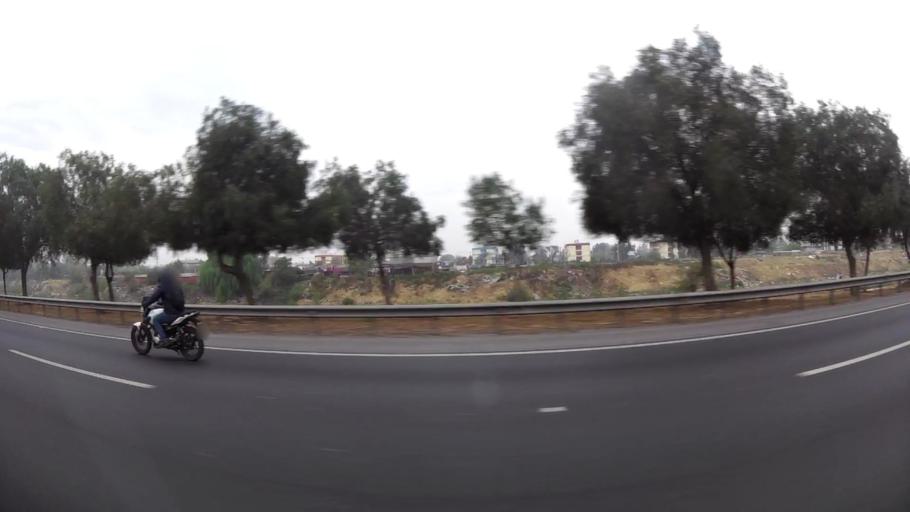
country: CL
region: Santiago Metropolitan
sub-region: Provincia de Santiago
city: Lo Prado
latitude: -33.4117
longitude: -70.7367
